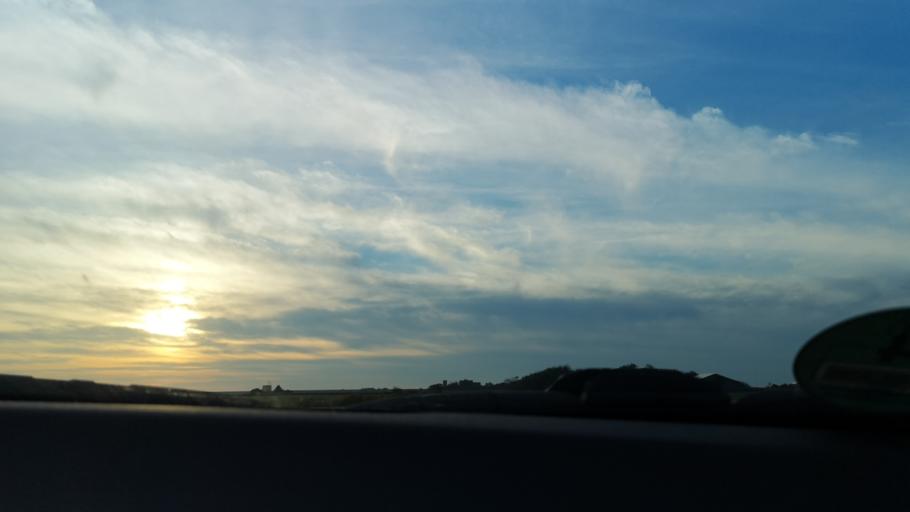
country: DE
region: Schleswig-Holstein
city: Pellworm
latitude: 54.5155
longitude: 8.6233
